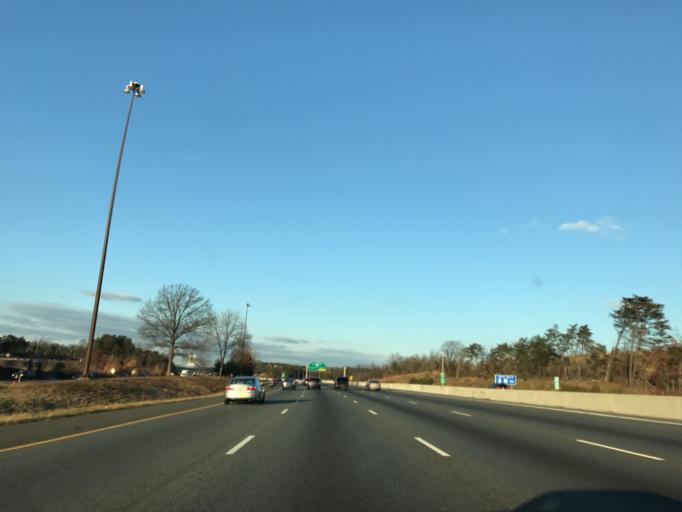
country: US
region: Maryland
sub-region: Prince George's County
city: West Laurel
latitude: 39.0893
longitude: -76.8935
